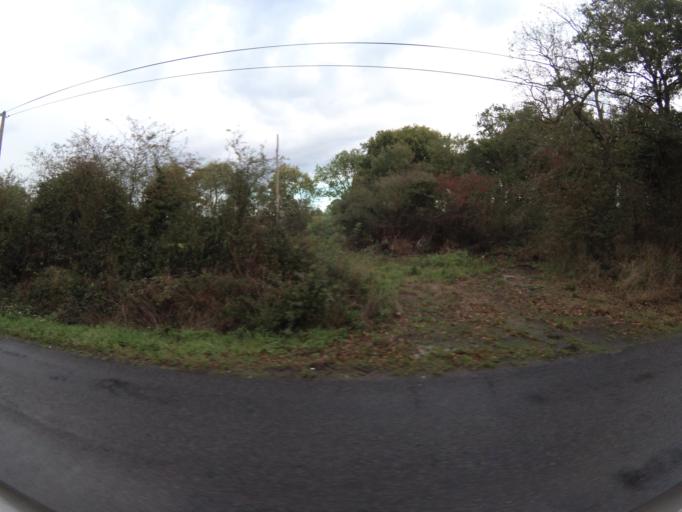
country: FR
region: Pays de la Loire
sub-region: Departement de la Loire-Atlantique
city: Saint-Hilaire-de-Clisson
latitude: 47.0665
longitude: -1.3161
